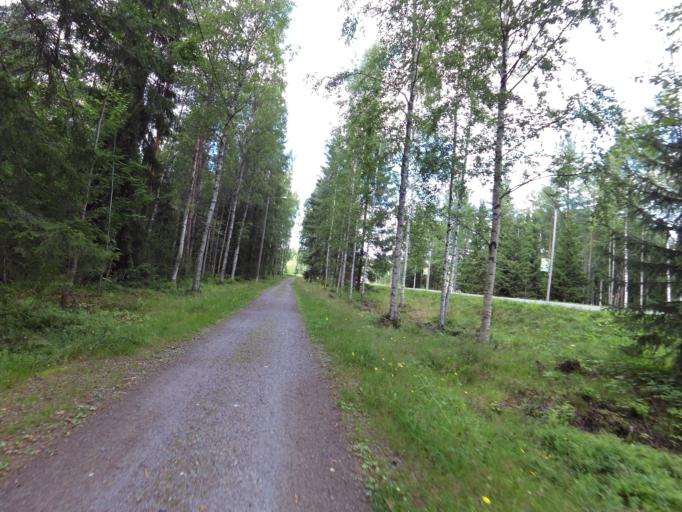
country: FI
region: Pirkanmaa
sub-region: Tampere
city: Yloejaervi
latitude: 61.5125
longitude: 23.6175
